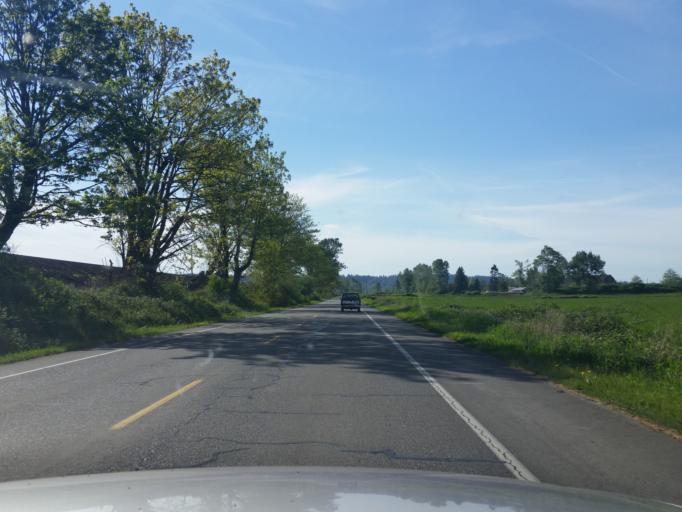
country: US
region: Washington
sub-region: Snohomish County
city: Fobes Hill
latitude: 47.9181
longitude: -122.1388
